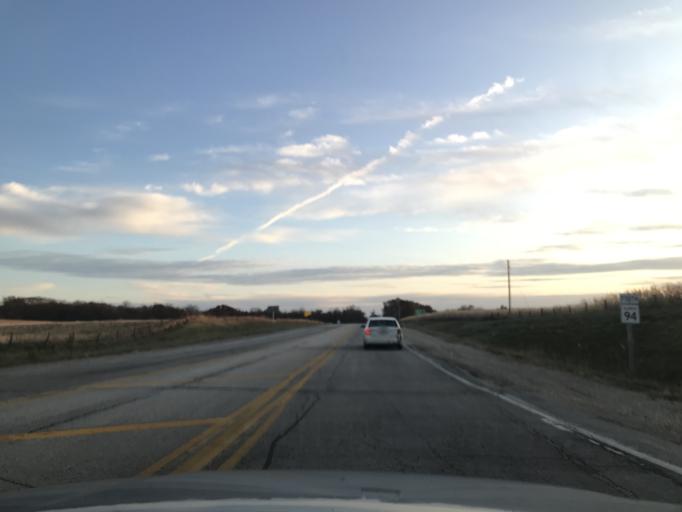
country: US
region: Illinois
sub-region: Henderson County
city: Oquawka
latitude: 40.9234
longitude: -90.8642
